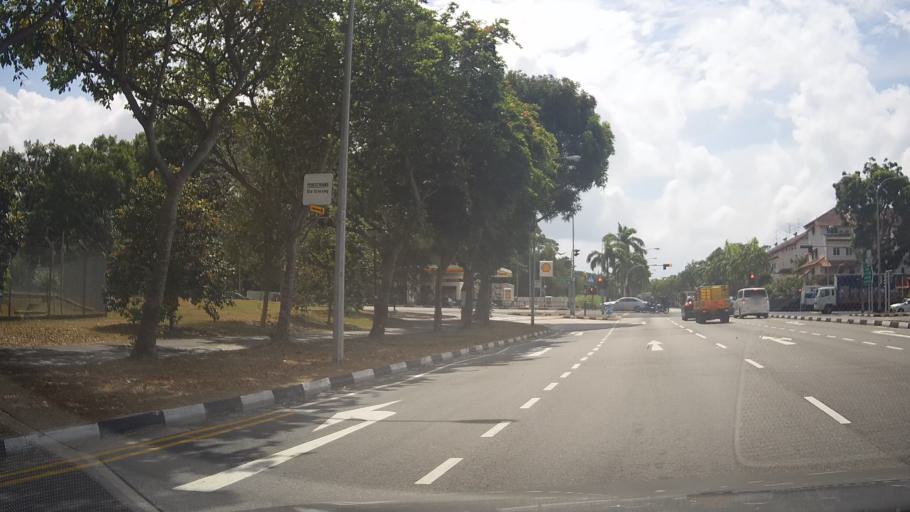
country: MY
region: Johor
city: Kampung Pasir Gudang Baru
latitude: 1.3664
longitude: 103.9661
